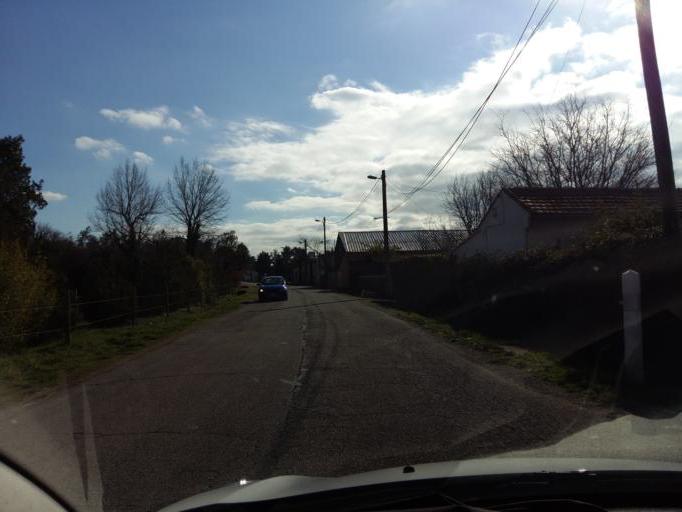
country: FR
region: Provence-Alpes-Cote d'Azur
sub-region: Departement du Vaucluse
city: Cavaillon
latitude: 43.8246
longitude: 5.0474
